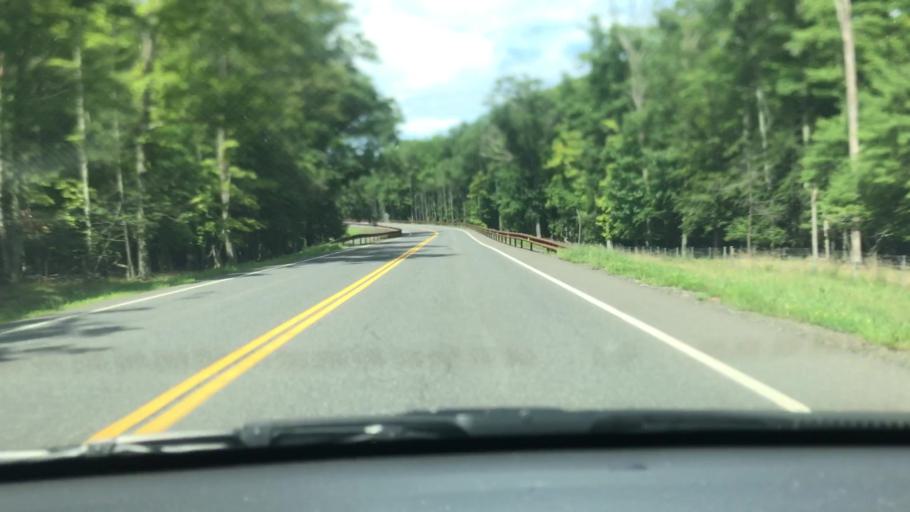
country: US
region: New York
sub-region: Ulster County
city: Shokan
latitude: 41.9357
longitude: -74.2141
